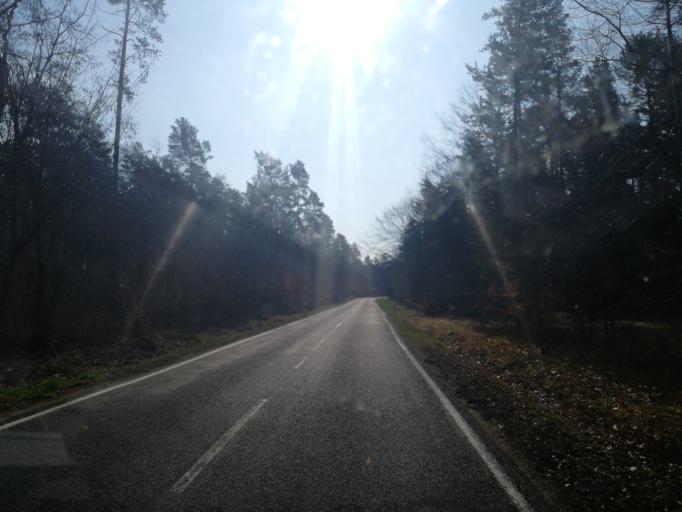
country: DE
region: Brandenburg
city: Sonnewalde
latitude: 51.7706
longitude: 13.6479
